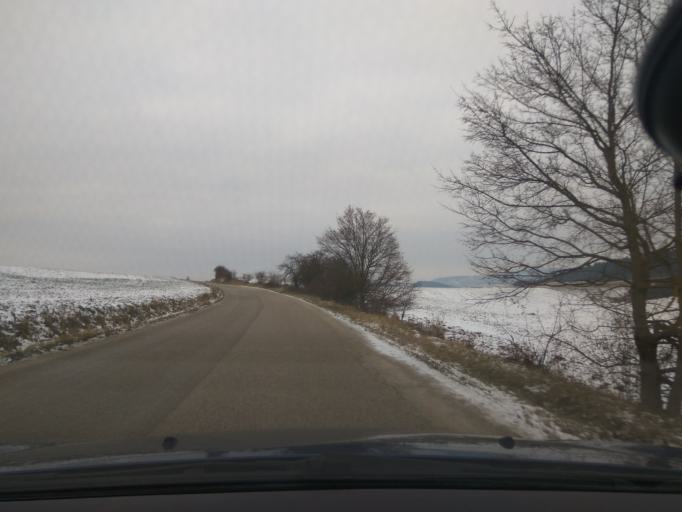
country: SK
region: Nitriansky
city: Stara Tura
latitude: 48.7921
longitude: 17.7301
